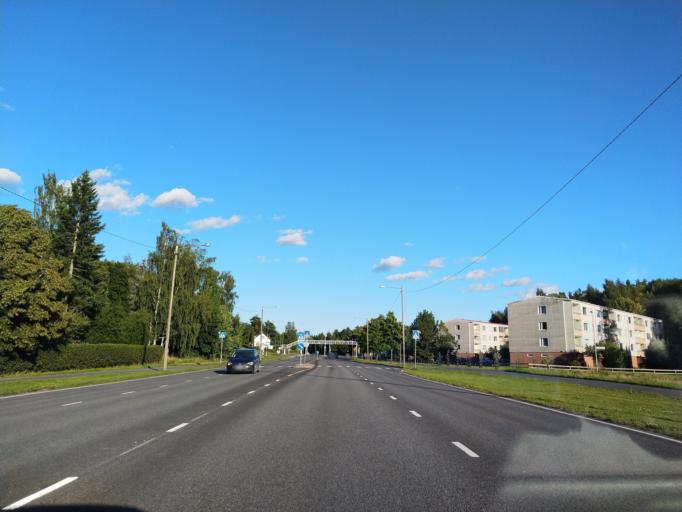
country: FI
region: Varsinais-Suomi
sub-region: Turku
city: Kaarina
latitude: 60.4450
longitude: 22.3292
